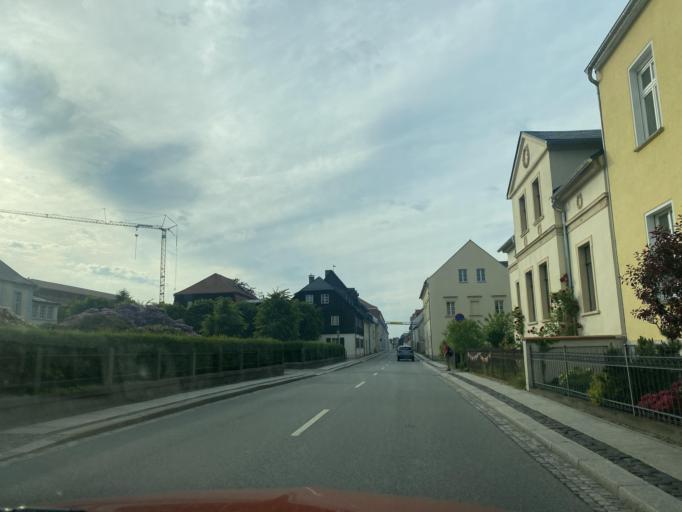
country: DE
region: Saxony
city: Herrnhut
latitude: 51.0140
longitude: 14.7458
